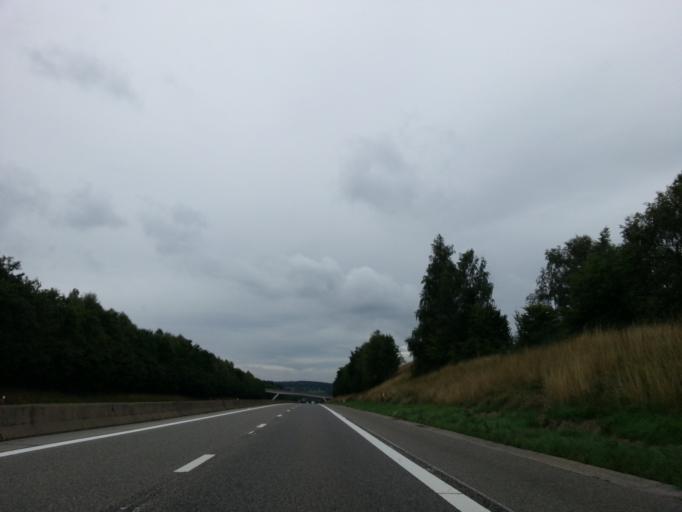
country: BE
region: Wallonia
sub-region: Province de Liege
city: Malmedy
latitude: 50.3602
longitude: 6.0449
